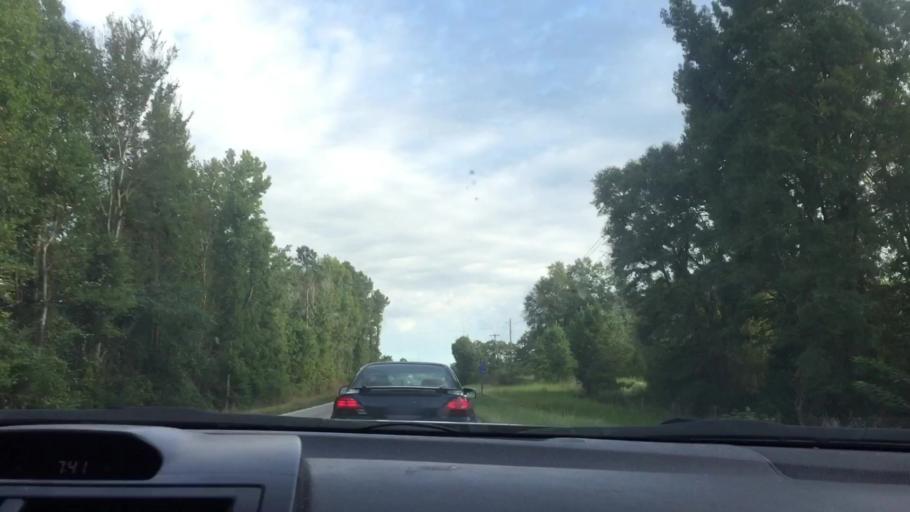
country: US
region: Alabama
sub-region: Hale County
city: Moundville
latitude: 32.9536
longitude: -87.6233
